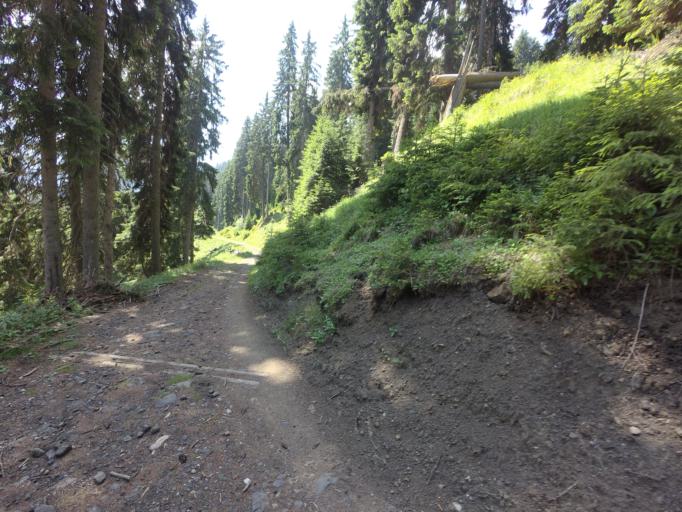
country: IT
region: Trentino-Alto Adige
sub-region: Bolzano
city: Ortisei
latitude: 46.5223
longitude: 11.6589
